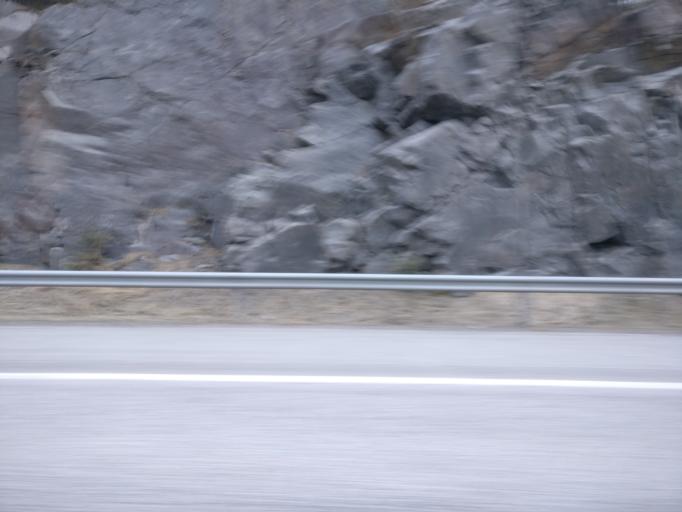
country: FI
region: Haeme
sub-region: Riihimaeki
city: Riihimaeki
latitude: 60.6676
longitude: 24.7839
